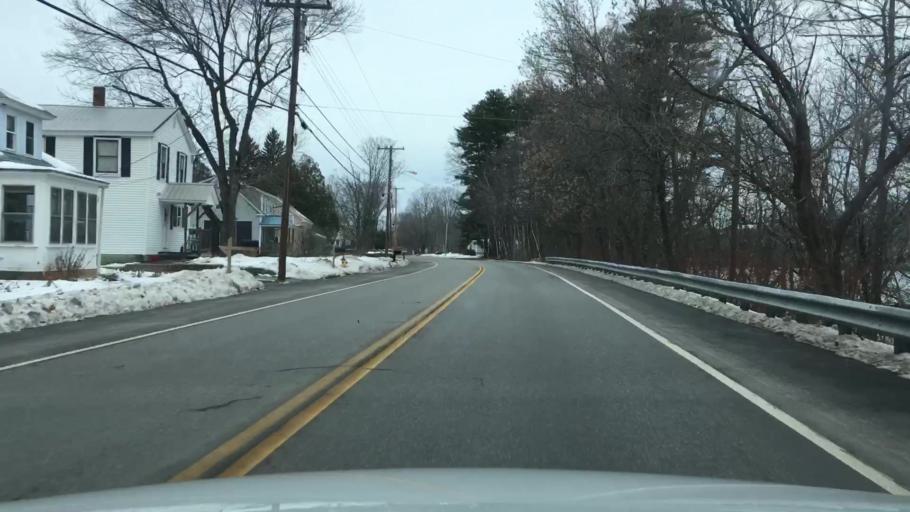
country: US
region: Maine
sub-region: Androscoggin County
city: Lewiston
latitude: 44.0720
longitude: -70.2090
